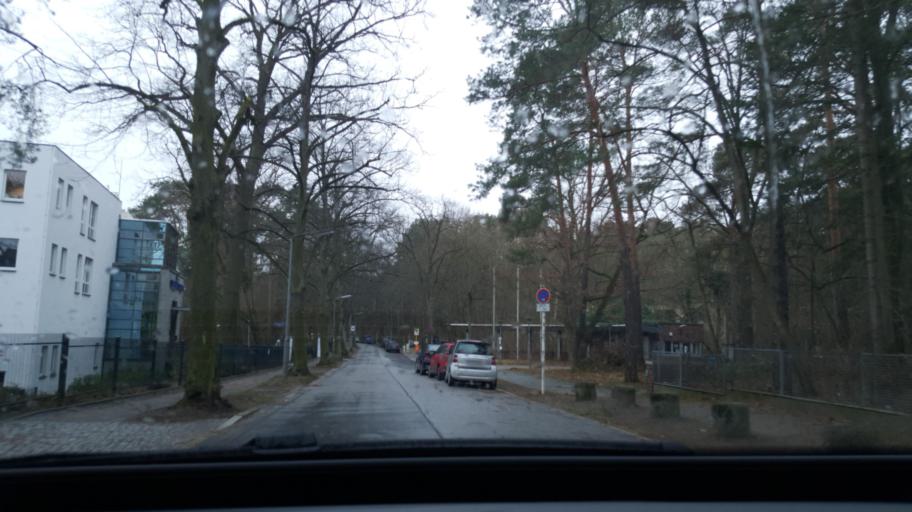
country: DE
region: Berlin
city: Wannsee
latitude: 52.4312
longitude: 13.1617
